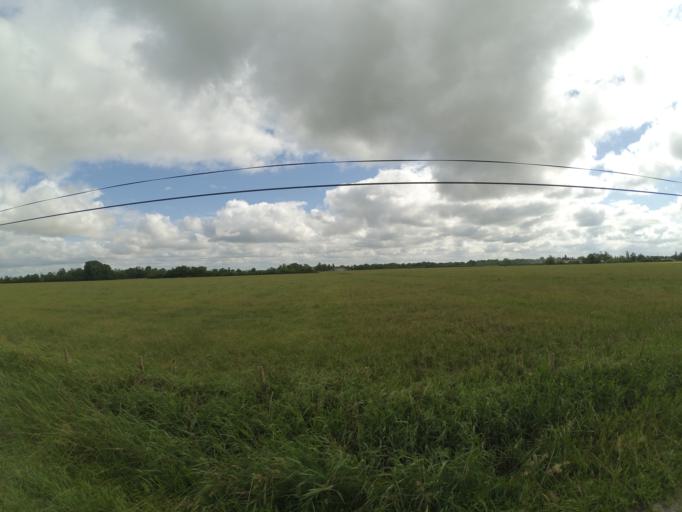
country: FR
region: Aquitaine
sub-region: Departement de la Gironde
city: Ludon-Medoc
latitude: 44.9894
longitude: -0.5822
